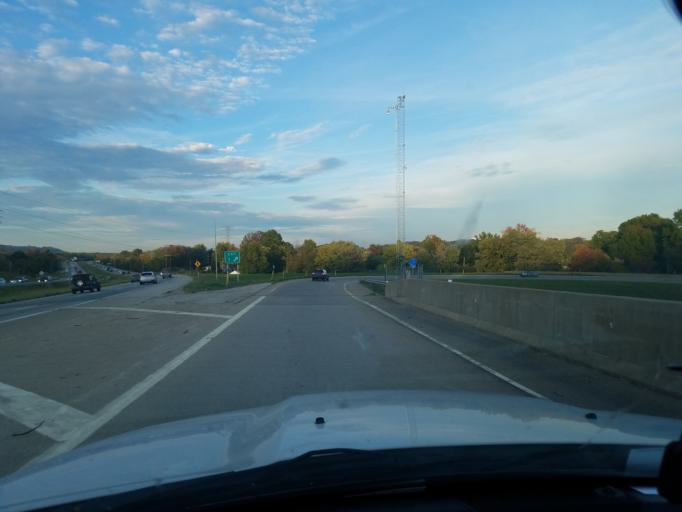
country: US
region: Indiana
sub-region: Floyd County
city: New Albany
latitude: 38.3107
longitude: -85.8456
